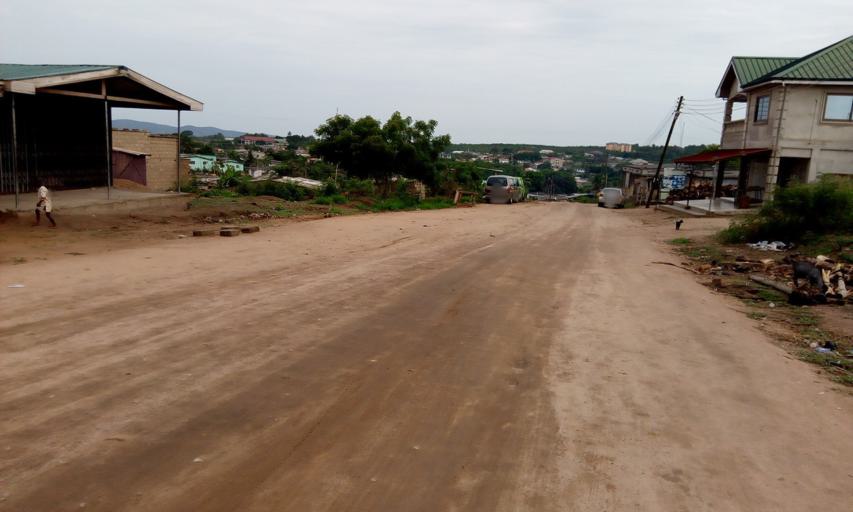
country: GH
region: Central
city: Winneba
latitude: 5.3547
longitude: -0.6159
